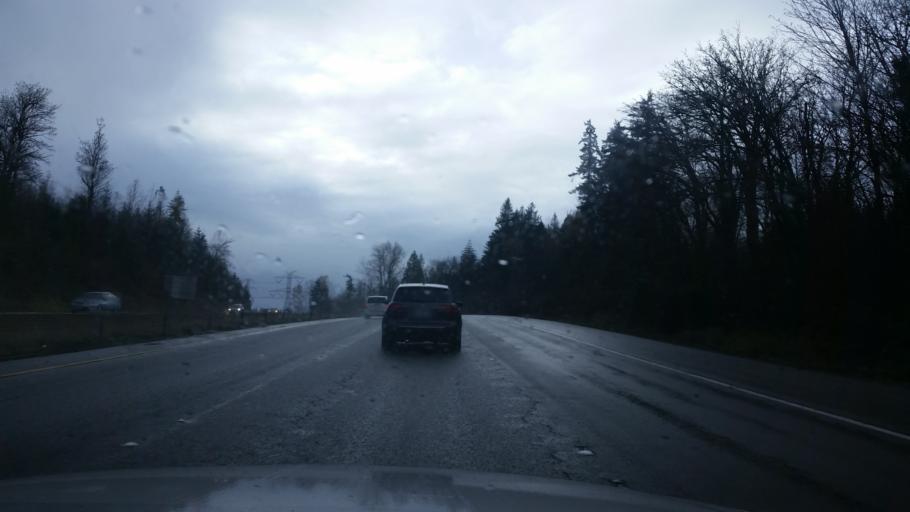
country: US
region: Washington
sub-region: King County
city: Covington
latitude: 47.3463
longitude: -122.1422
